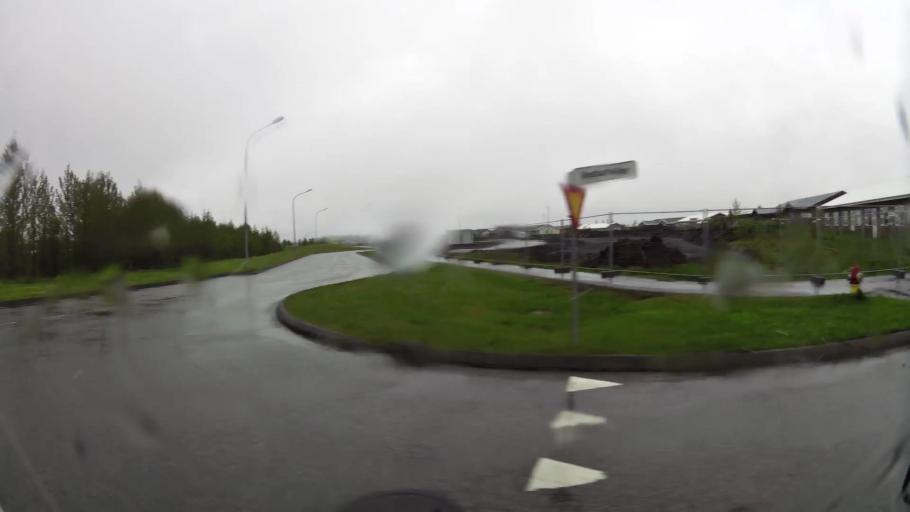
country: IS
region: South
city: Selfoss
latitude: 63.9262
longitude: -21.0065
